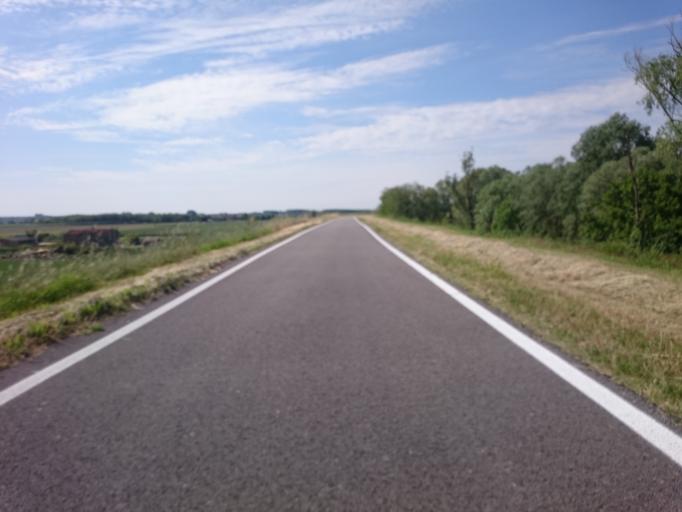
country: IT
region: Veneto
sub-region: Provincia di Rovigo
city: Corbola
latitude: 44.9880
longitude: 12.0897
